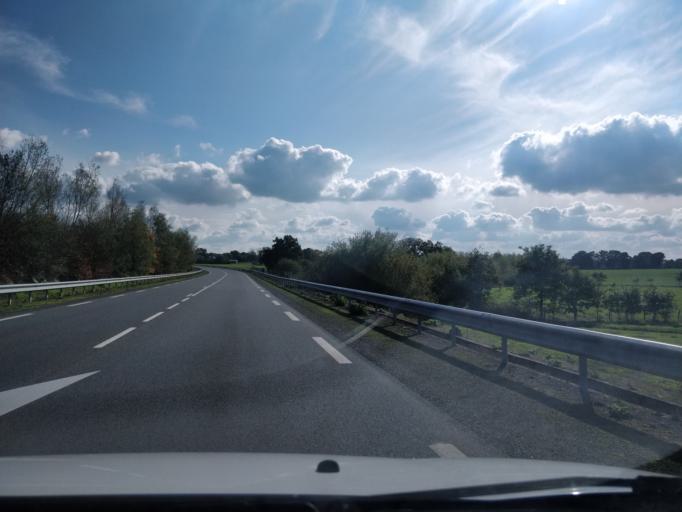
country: FR
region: Brittany
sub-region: Departement d'Ille-et-Vilaine
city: Saint-Aubin-du-Cormier
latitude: 48.2516
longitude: -1.4102
